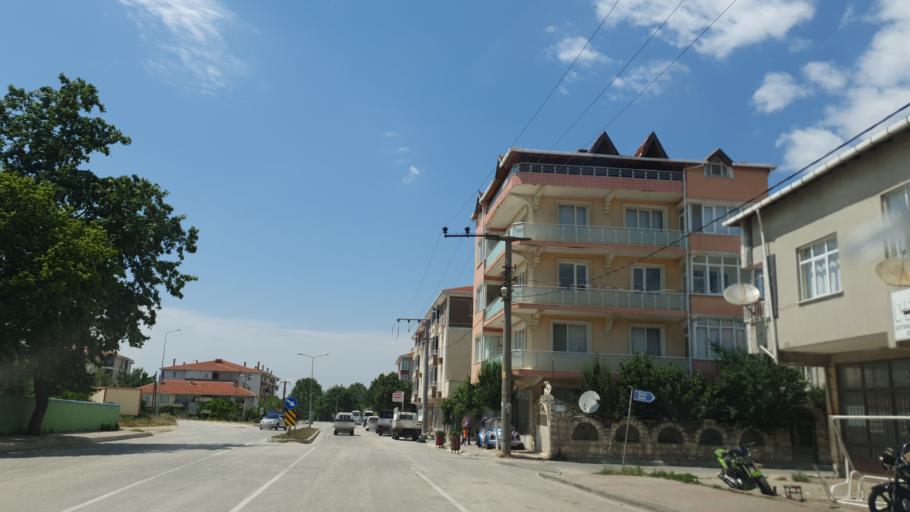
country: TR
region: Tekirdag
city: Saray
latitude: 41.4403
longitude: 27.9144
